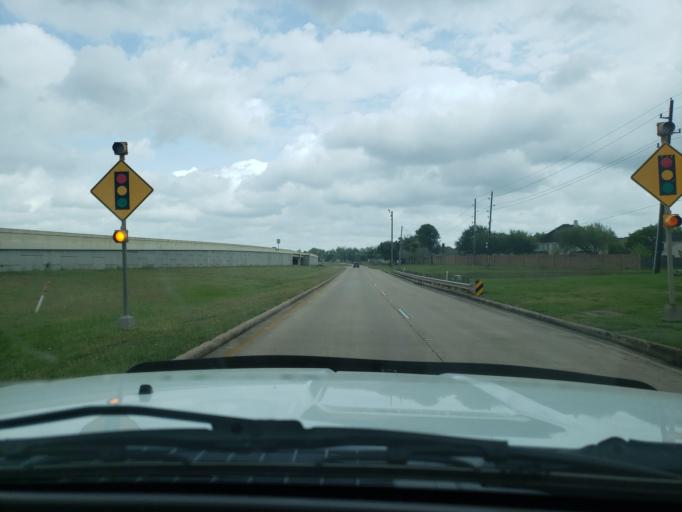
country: US
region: Texas
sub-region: Fort Bend County
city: Greatwood
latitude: 29.5722
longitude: -95.6822
